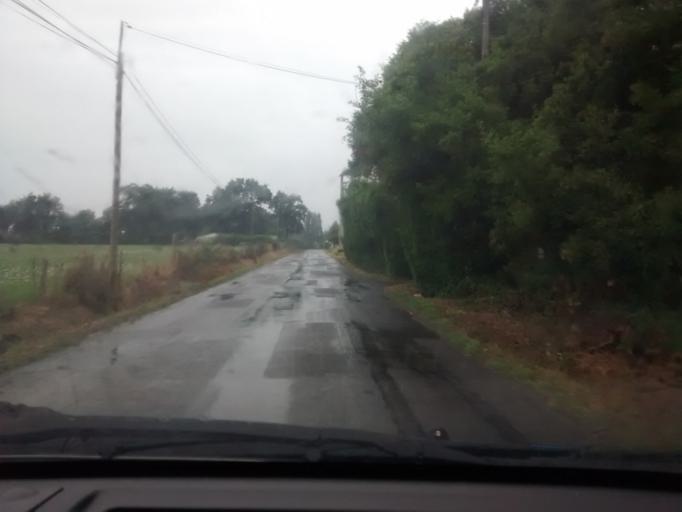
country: FR
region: Brittany
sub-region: Departement d'Ille-et-Vilaine
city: Betton
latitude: 48.1770
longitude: -1.6226
